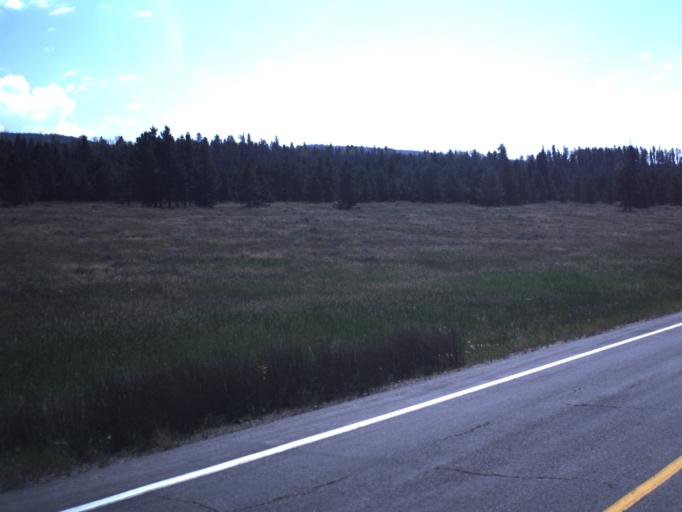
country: US
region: Utah
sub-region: Uintah County
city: Maeser
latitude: 40.7807
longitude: -109.4706
